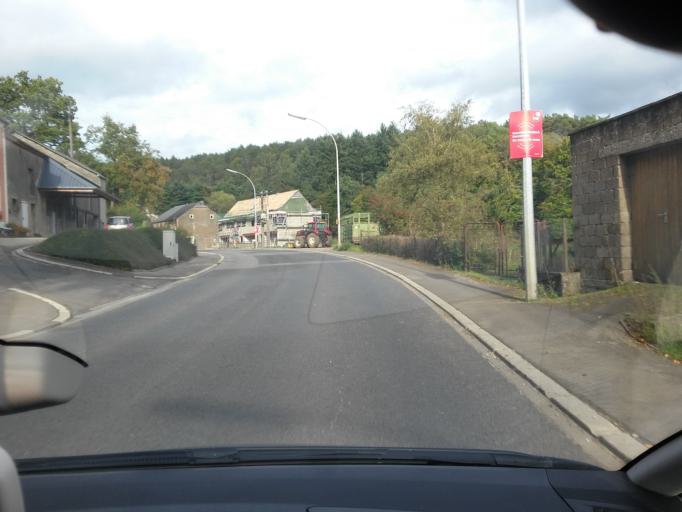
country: LU
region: Luxembourg
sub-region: Canton de Capellen
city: Hobscheid
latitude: 49.6905
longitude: 5.9152
